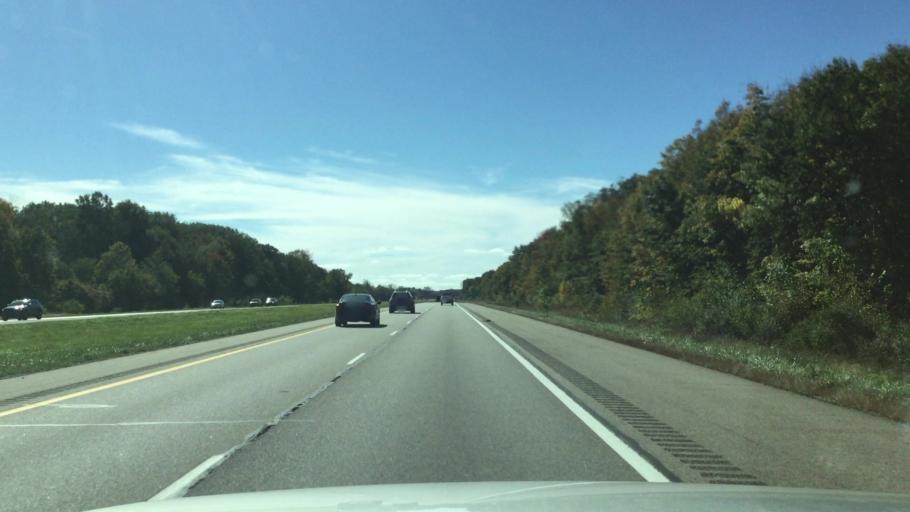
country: US
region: Michigan
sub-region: Washtenaw County
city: Ypsilanti
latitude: 42.3352
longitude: -83.6139
